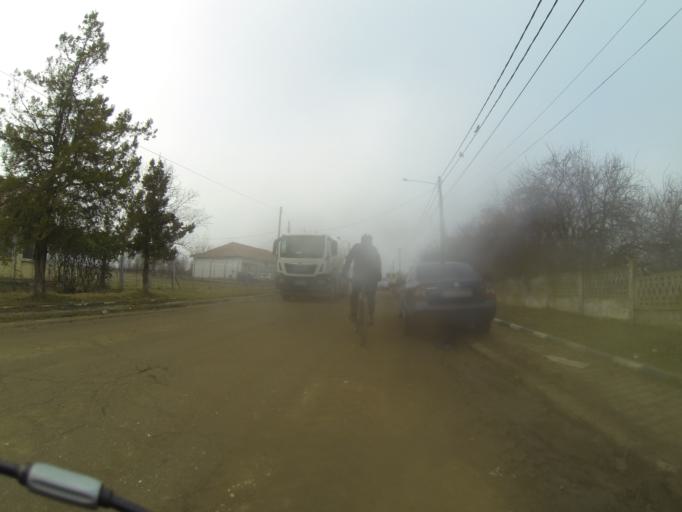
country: RO
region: Mehedinti
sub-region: Comuna Baclesu
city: Baclesu
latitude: 44.4772
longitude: 23.1140
